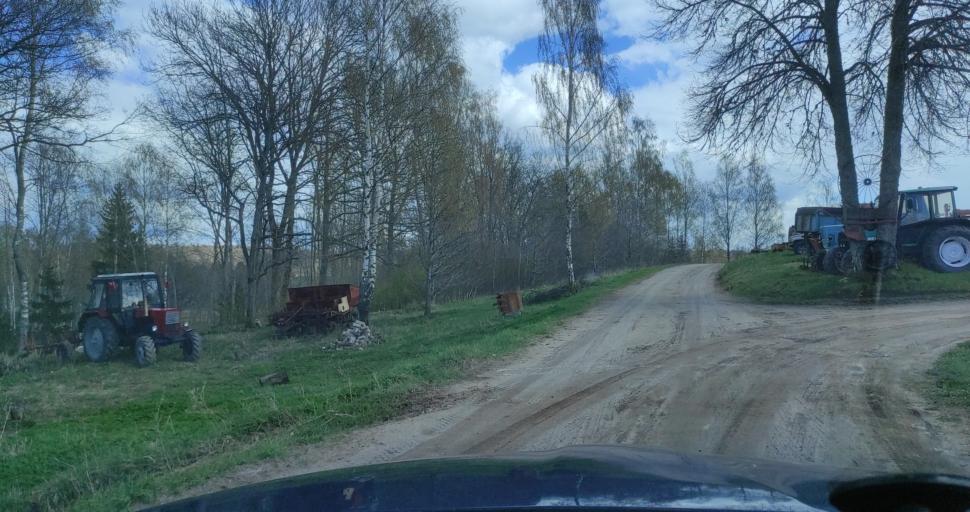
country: LV
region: Kuldigas Rajons
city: Kuldiga
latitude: 56.8601
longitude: 21.8361
